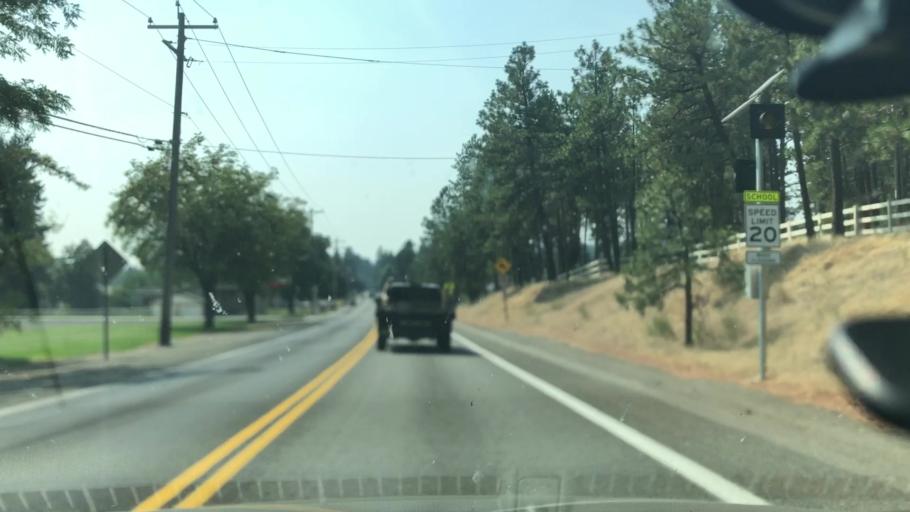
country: US
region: Washington
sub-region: Spokane County
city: Millwood
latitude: 47.6983
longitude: -117.2893
